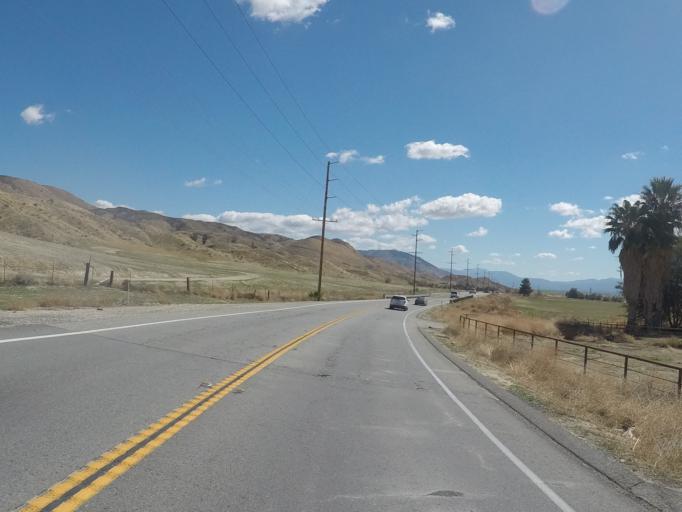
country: US
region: California
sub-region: Riverside County
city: Lakeview
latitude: 33.8885
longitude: -117.0682
